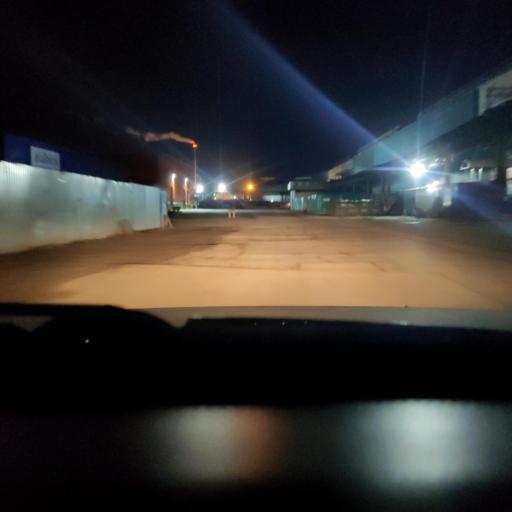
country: RU
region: Perm
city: Froly
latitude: 57.9618
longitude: 56.2765
